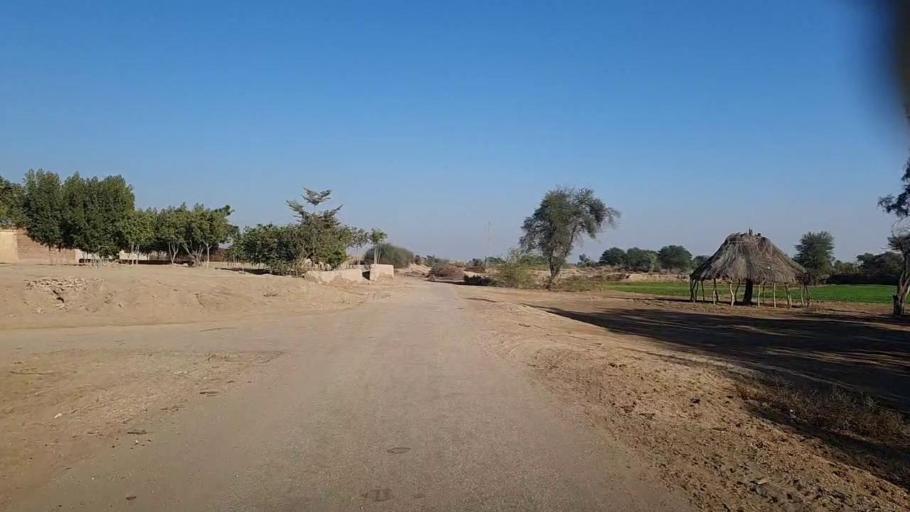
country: PK
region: Sindh
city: Khairpur
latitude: 27.8928
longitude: 69.7540
